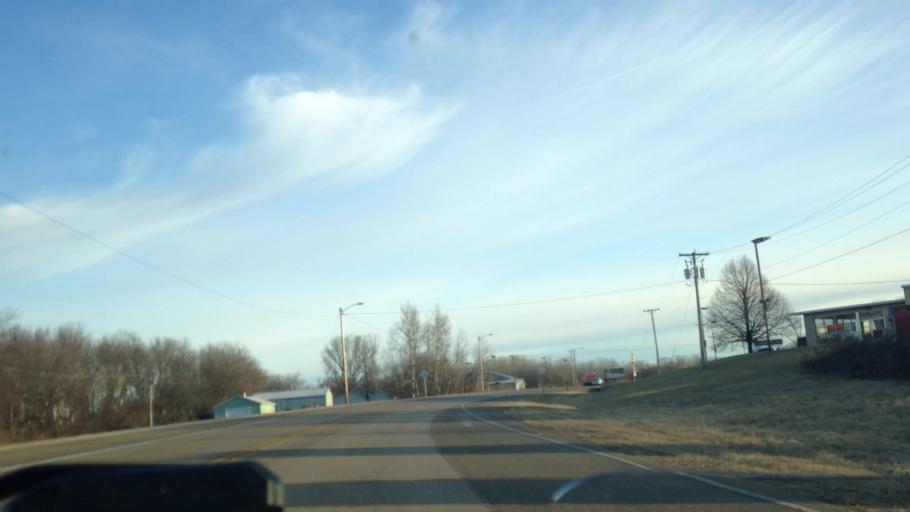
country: US
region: Wisconsin
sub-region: Dodge County
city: Mayville
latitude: 43.5095
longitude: -88.5408
